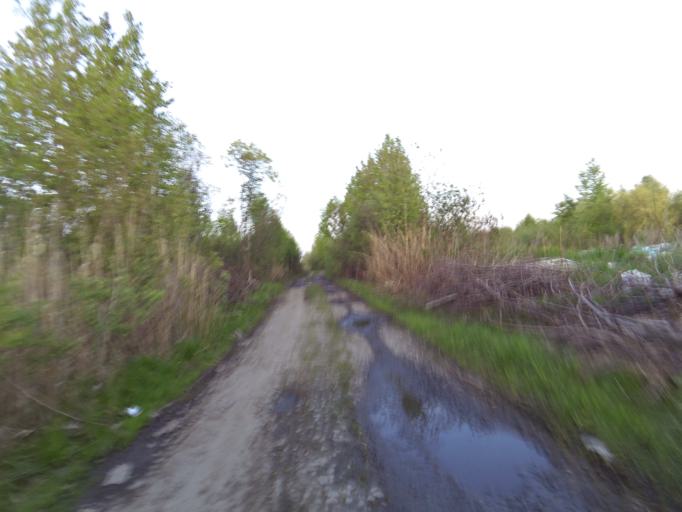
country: RU
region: Sverdlovsk
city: Shirokaya Rechka
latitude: 56.8387
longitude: 60.5124
